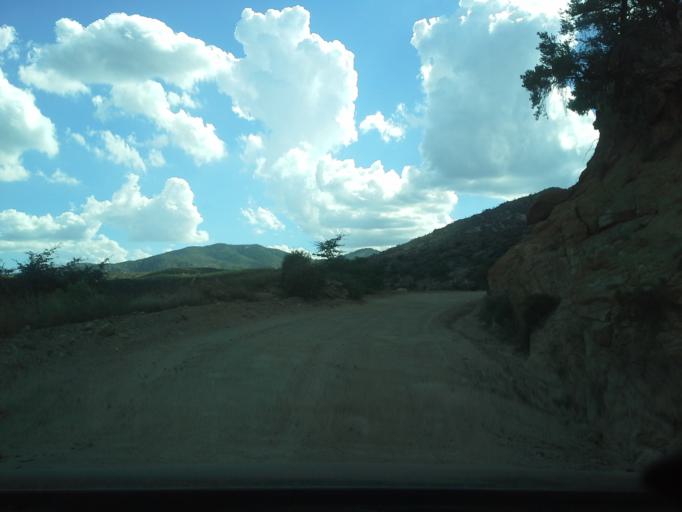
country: US
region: Arizona
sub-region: Yavapai County
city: Mayer
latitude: 34.2289
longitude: -112.3104
